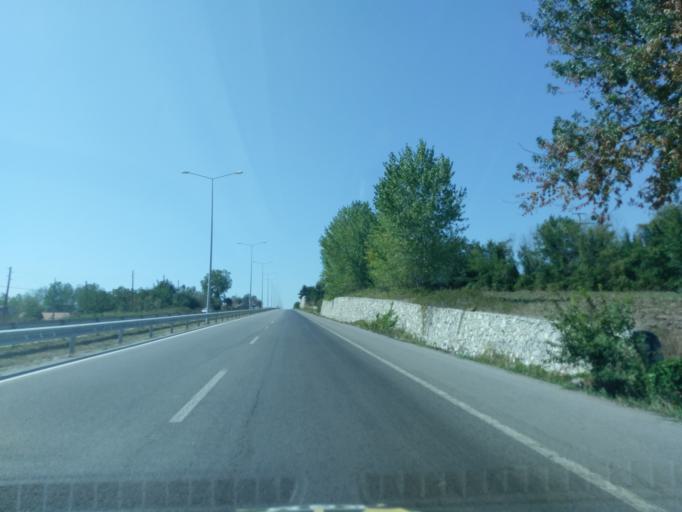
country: TR
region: Samsun
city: Ondokuzmayis
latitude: 41.5225
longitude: 35.9848
